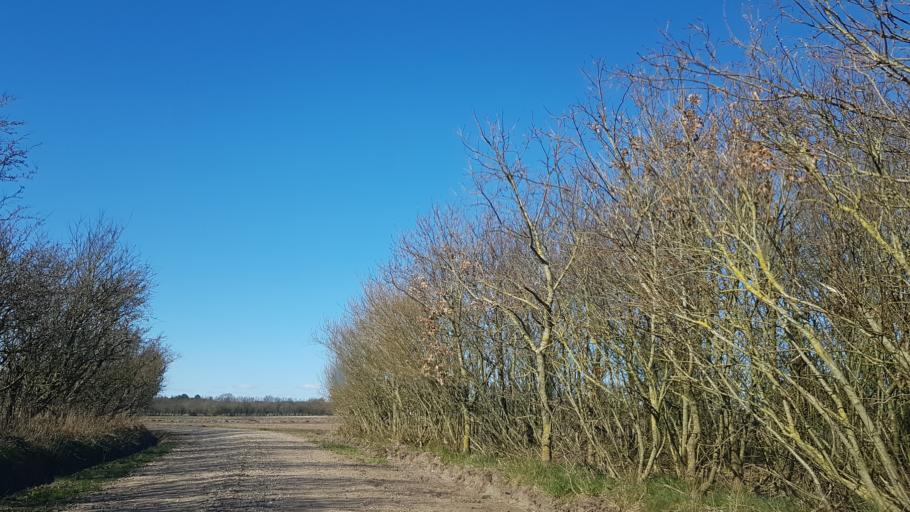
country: DK
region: South Denmark
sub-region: Esbjerg Kommune
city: Ribe
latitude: 55.2488
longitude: 8.7098
